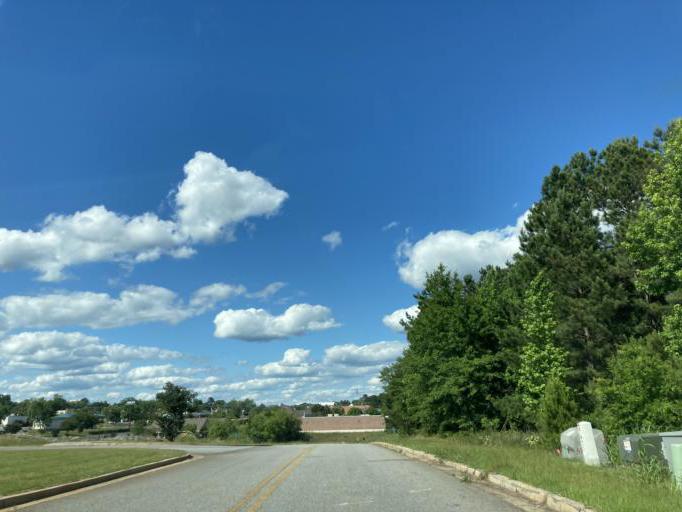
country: US
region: Georgia
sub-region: Jones County
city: Gray
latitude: 33.0000
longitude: -83.5490
